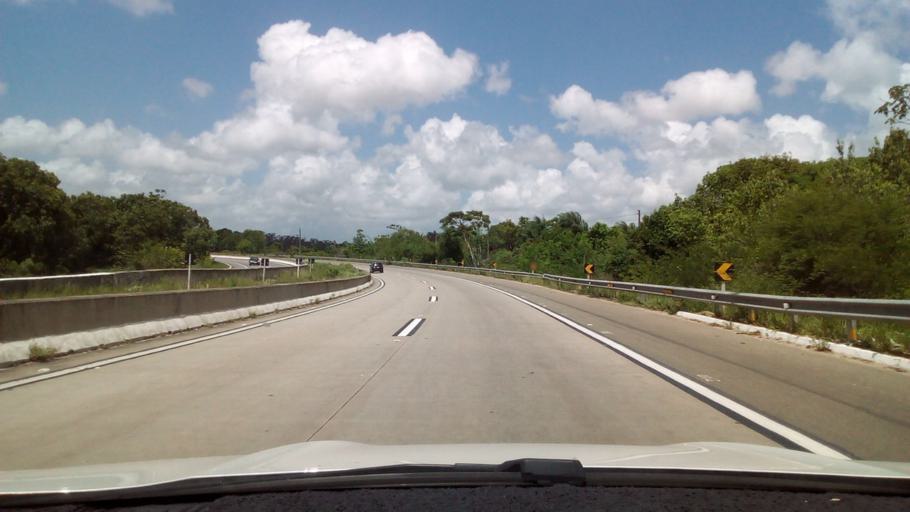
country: BR
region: Paraiba
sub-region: Conde
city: Conde
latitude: -7.2987
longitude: -34.9377
